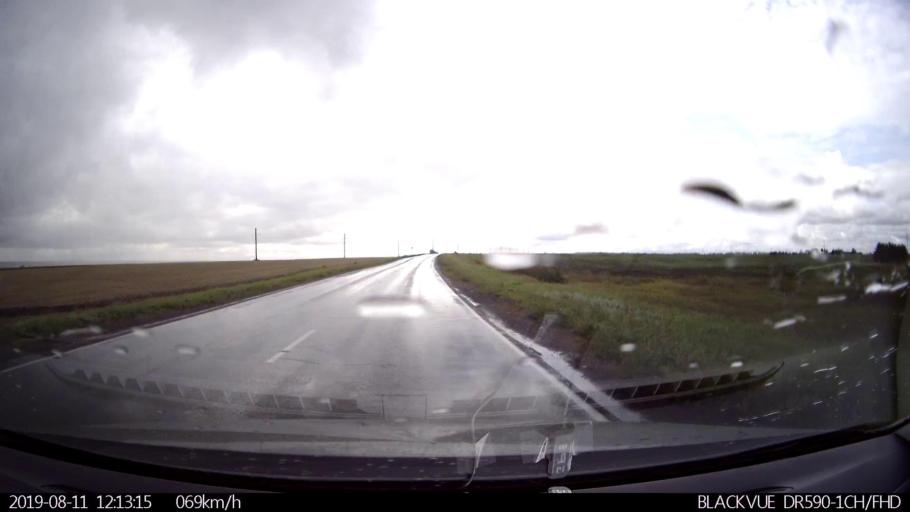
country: RU
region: Ulyanovsk
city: Silikatnyy
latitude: 53.9638
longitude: 47.9932
